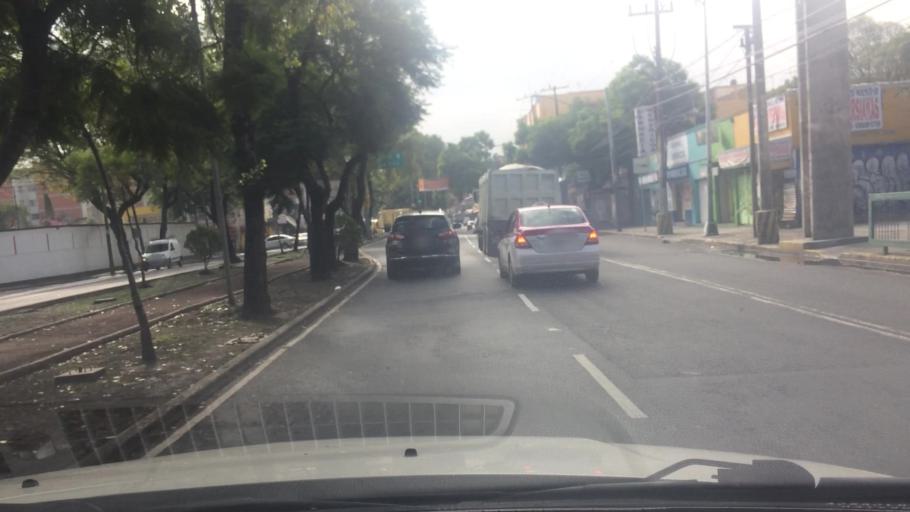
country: MX
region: Mexico City
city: Coyoacan
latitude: 19.3377
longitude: -99.1235
